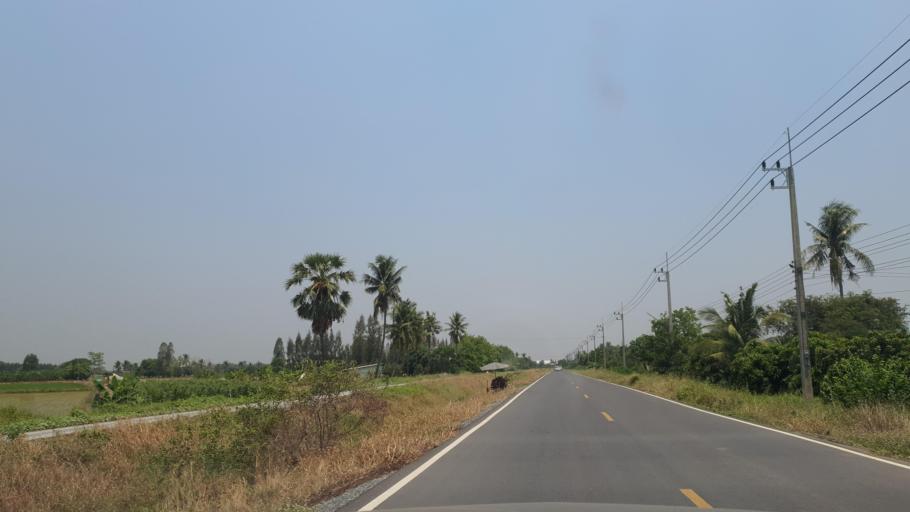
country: TH
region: Suphan Buri
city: Si Prachan
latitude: 14.5919
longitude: 100.1048
